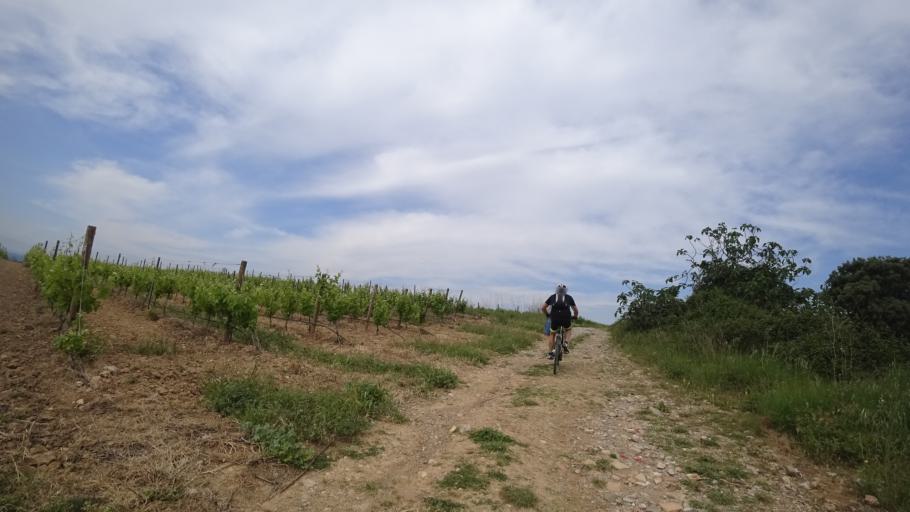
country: FR
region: Languedoc-Roussillon
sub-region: Departement de l'Aude
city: Canet
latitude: 43.2559
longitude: 2.8210
